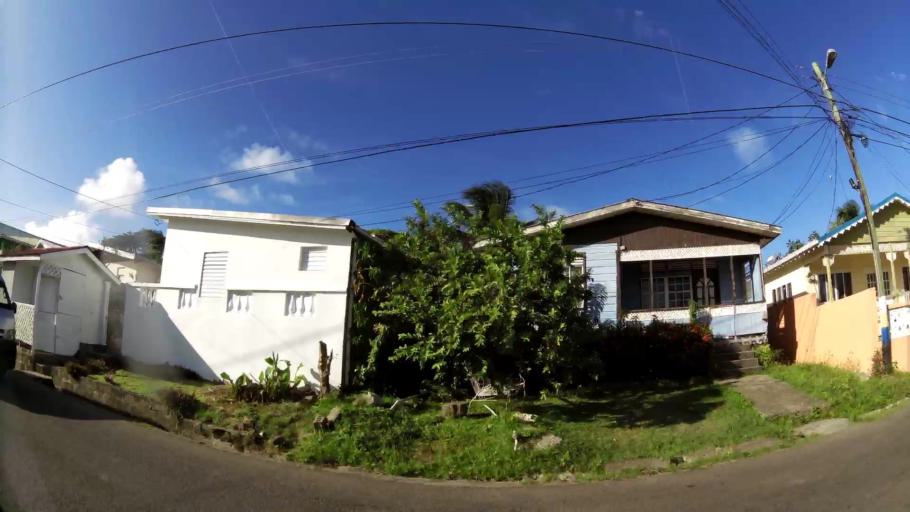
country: LC
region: Gros-Islet
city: Gros Islet
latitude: 14.0810
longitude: -60.9486
